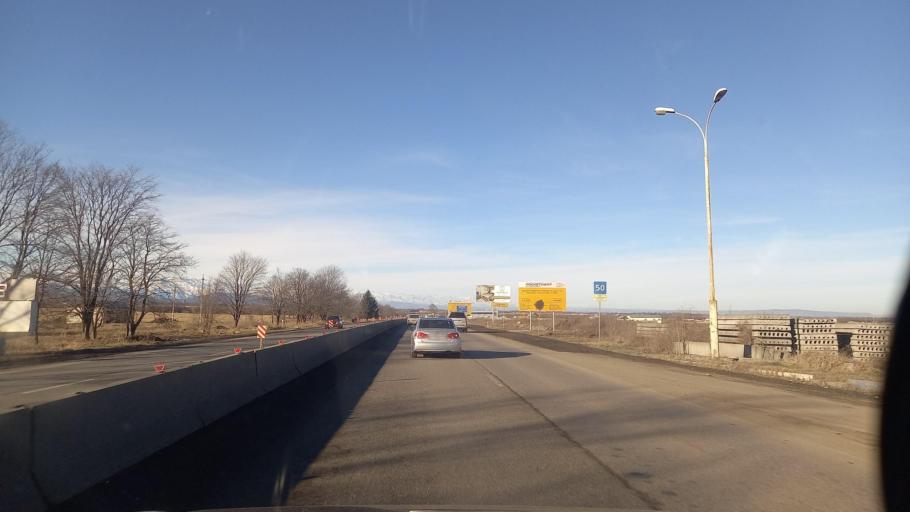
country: RU
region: North Ossetia
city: Vladikavkaz
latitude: 43.0255
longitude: 44.6255
